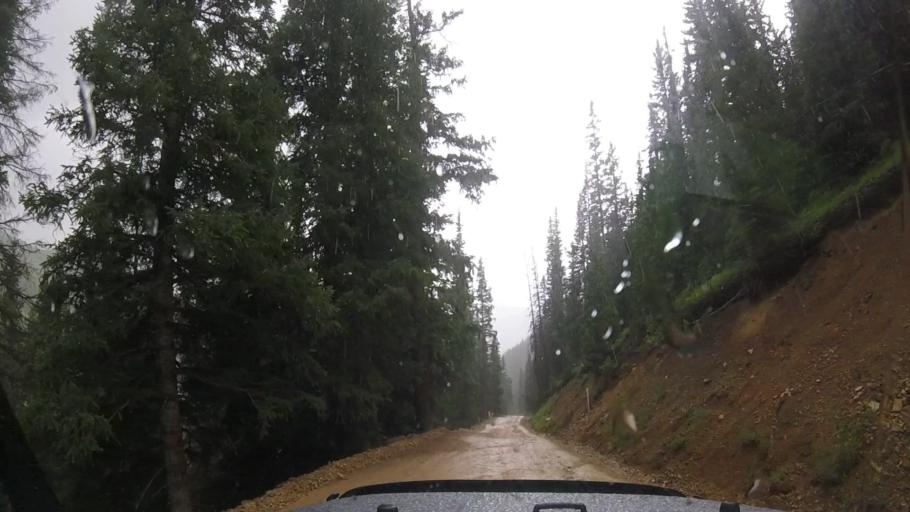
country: US
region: Colorado
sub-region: San Juan County
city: Silverton
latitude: 37.9049
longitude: -107.6467
